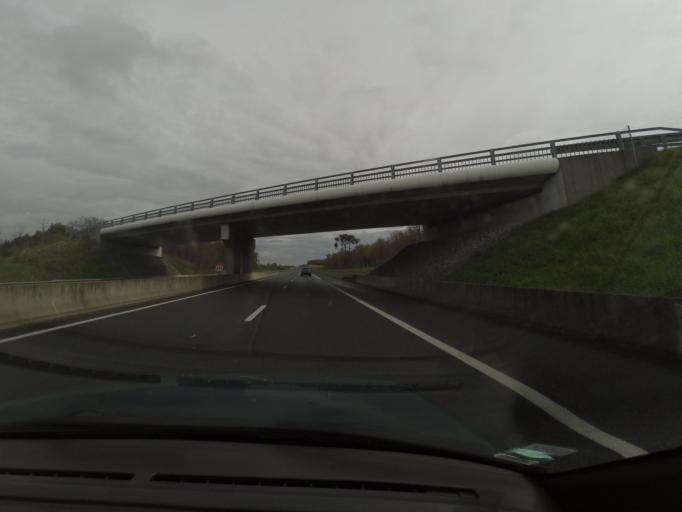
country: FR
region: Pays de la Loire
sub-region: Departement de Maine-et-Loire
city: Saint-Lambert-la-Potherie
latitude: 47.4742
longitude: -0.6768
